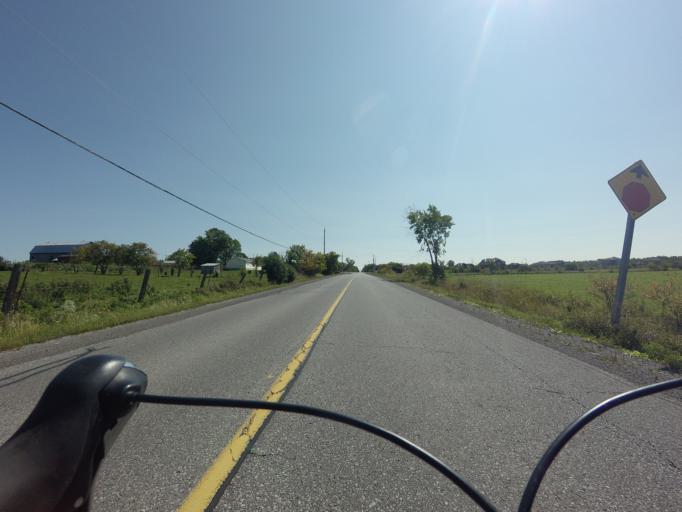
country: CA
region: Ontario
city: Bells Corners
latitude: 45.3877
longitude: -76.0013
